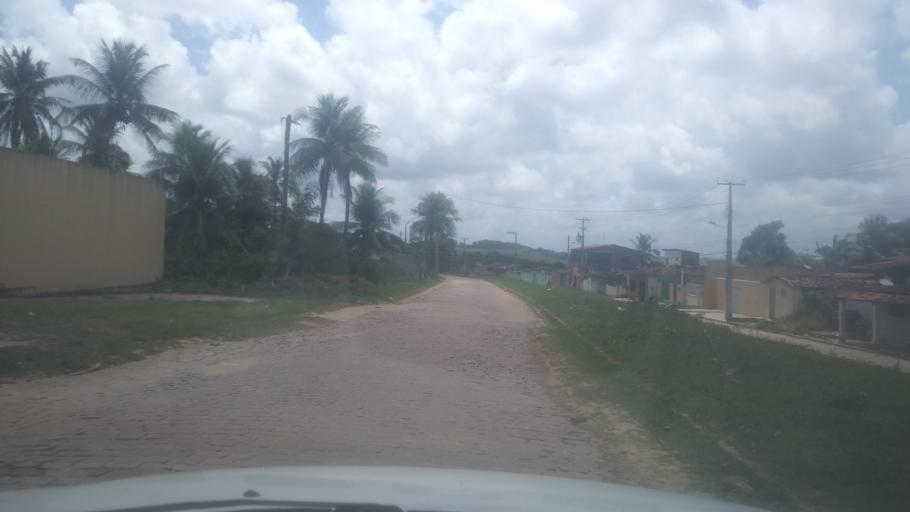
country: BR
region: Rio Grande do Norte
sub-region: Sao Jose De Mipibu
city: Sao Jose de Mipibu
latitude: -6.0705
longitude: -35.2345
